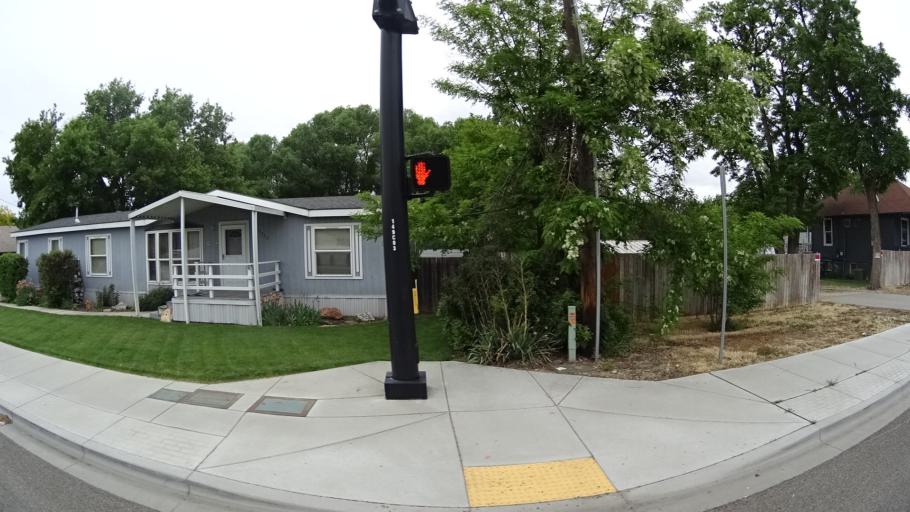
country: US
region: Idaho
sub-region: Ada County
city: Eagle
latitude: 43.6340
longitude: -116.3287
